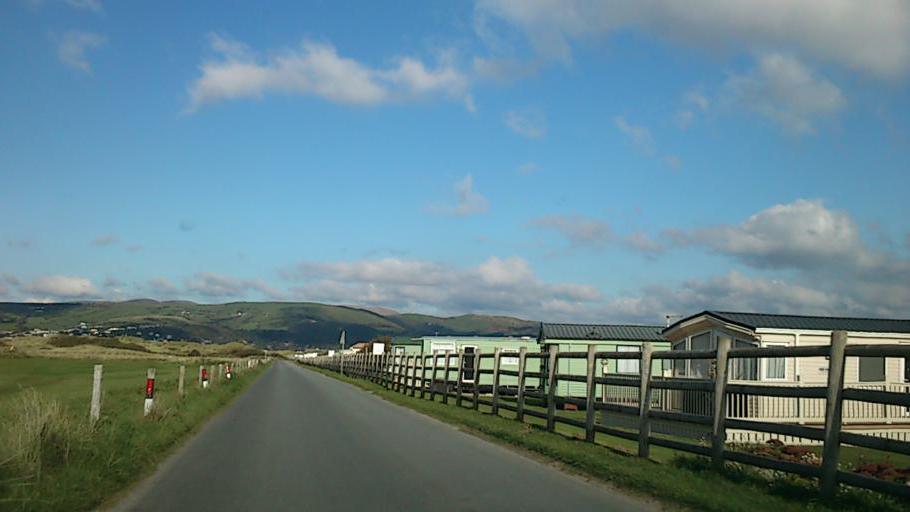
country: GB
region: Wales
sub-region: Gwynedd
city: Tywyn
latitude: 52.5213
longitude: -4.0538
